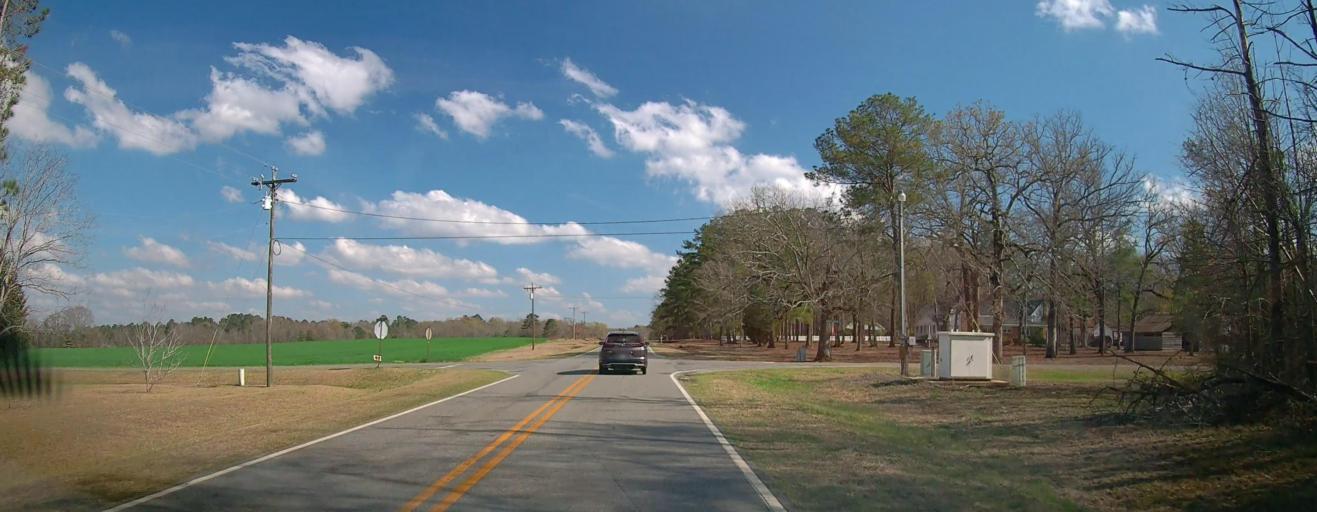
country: US
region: Georgia
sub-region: Wilkinson County
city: Irwinton
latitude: 32.6307
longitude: -83.1004
